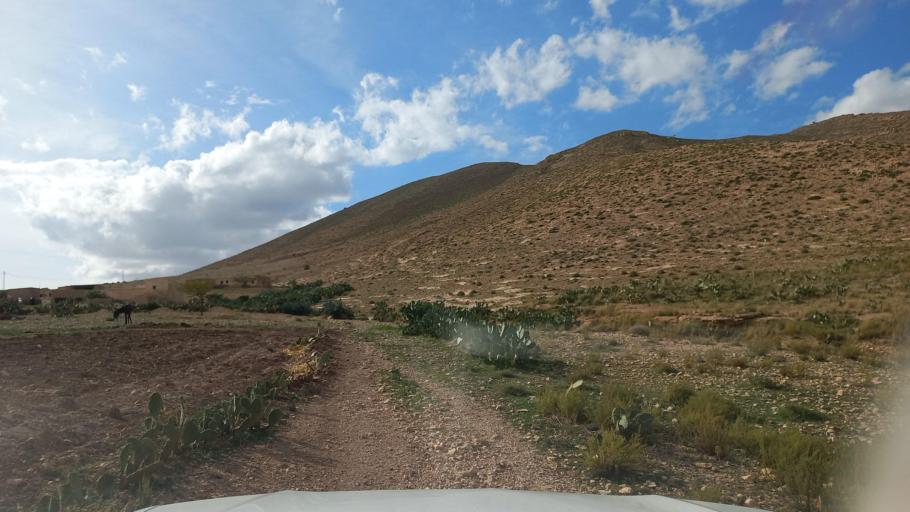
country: TN
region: Al Qasrayn
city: Sbiba
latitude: 35.4575
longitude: 9.0685
